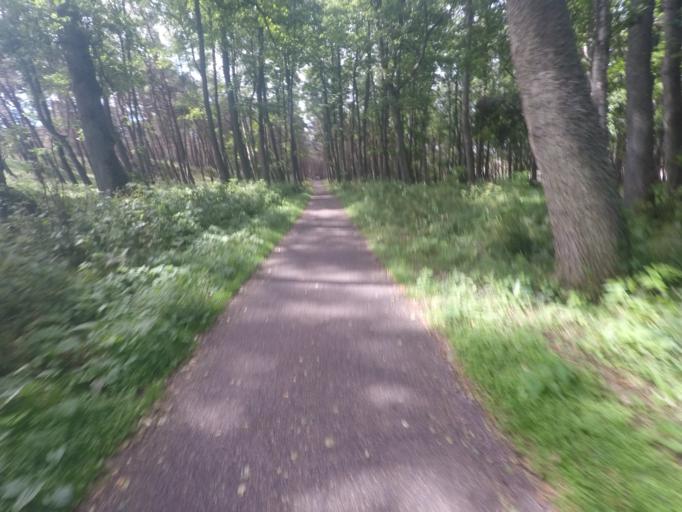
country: LT
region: Klaipedos apskritis
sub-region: Klaipeda
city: Klaipeda
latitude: 55.6619
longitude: 21.1077
